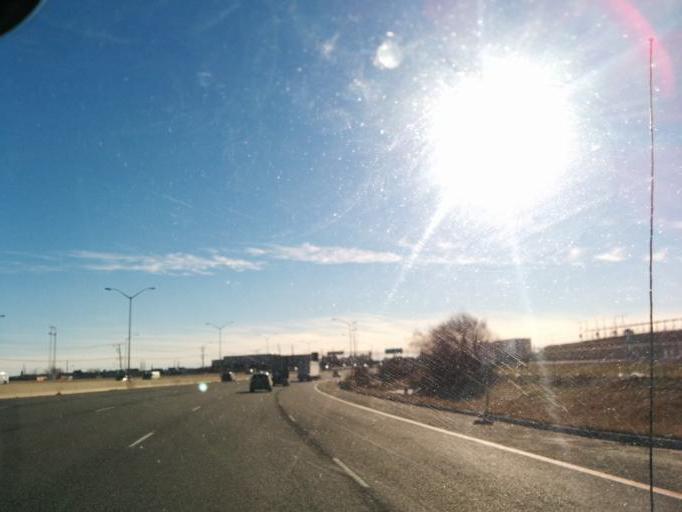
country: CA
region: Ontario
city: Etobicoke
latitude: 43.6821
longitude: -79.5953
